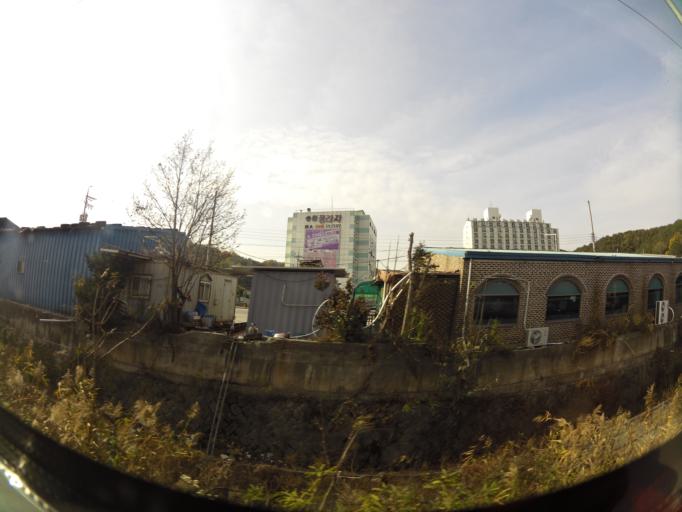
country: KR
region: Chungcheongbuk-do
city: Cheongju-si
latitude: 36.6141
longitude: 127.2934
